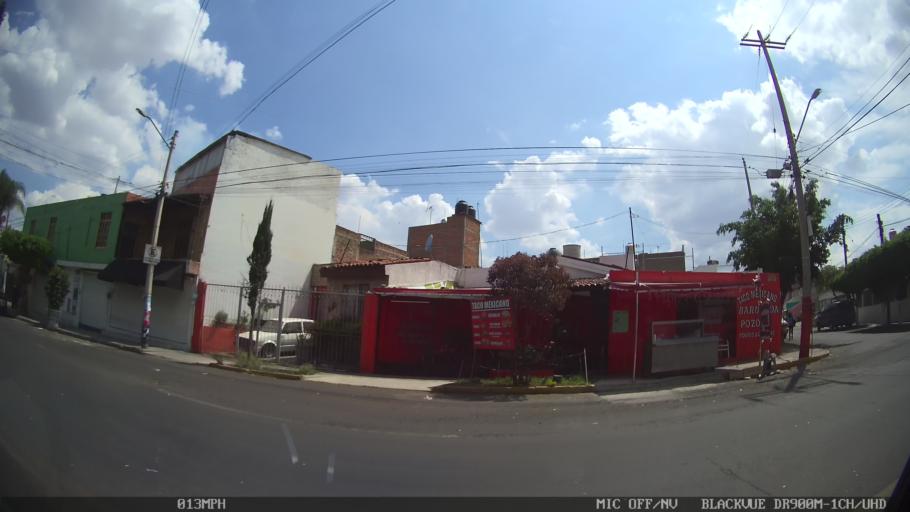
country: MX
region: Jalisco
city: Tonala
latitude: 20.6226
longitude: -103.2540
